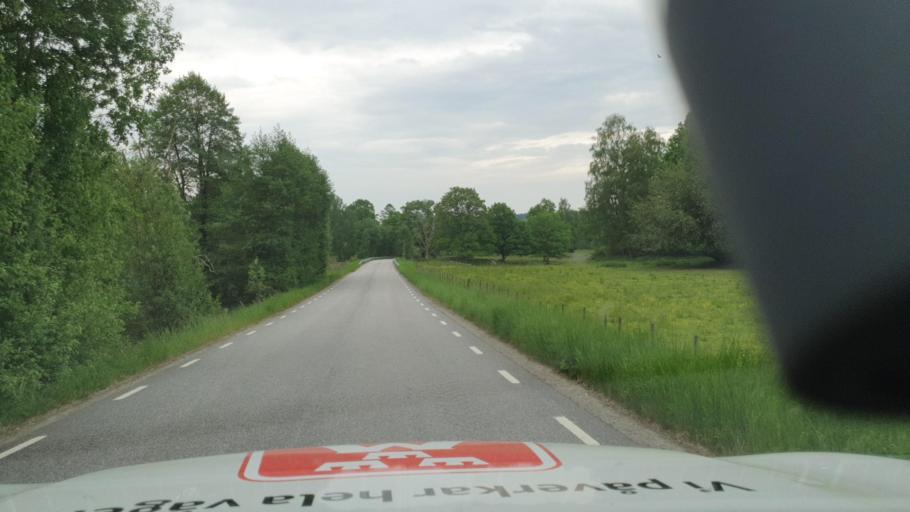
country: SE
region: Vaestra Goetaland
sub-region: Ulricehamns Kommun
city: Ulricehamn
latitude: 57.8528
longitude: 13.2852
